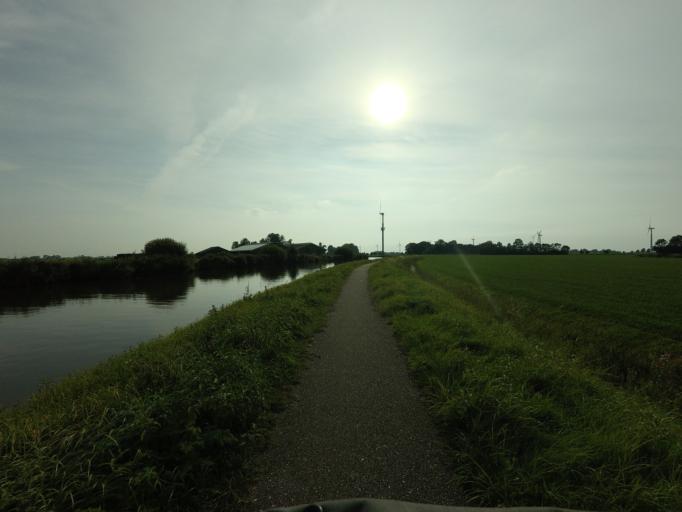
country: NL
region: Friesland
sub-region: Sudwest Fryslan
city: Bolsward
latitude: 53.0563
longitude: 5.5145
